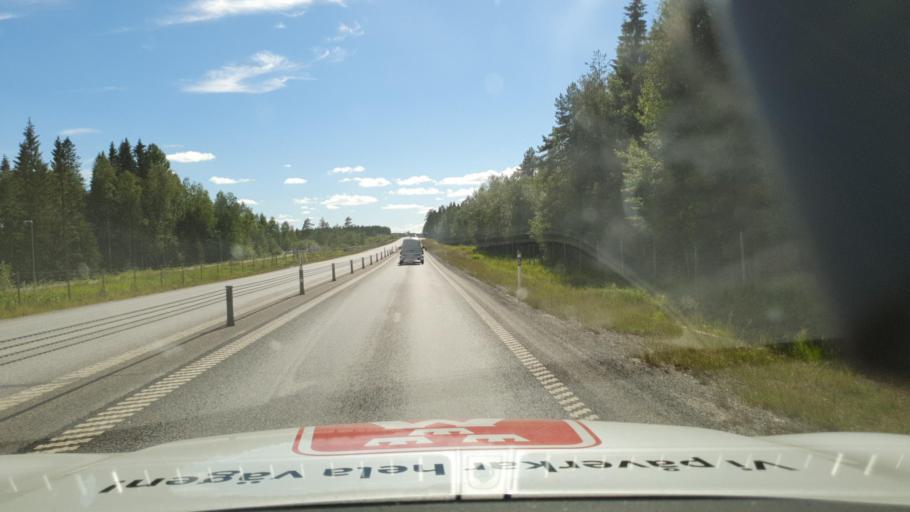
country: SE
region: Vaesterbotten
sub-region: Umea Kommun
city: Taftea
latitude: 63.8664
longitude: 20.4319
